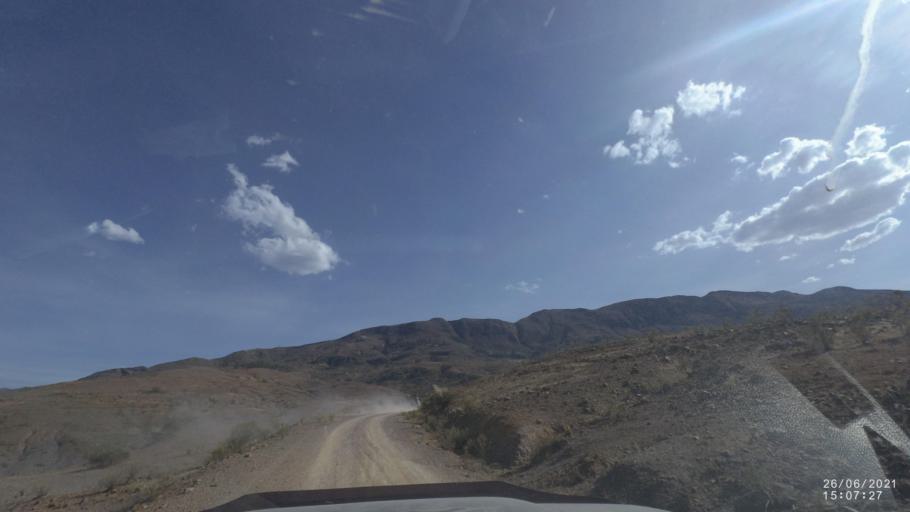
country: BO
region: Cochabamba
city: Mizque
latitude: -17.9434
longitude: -65.6374
